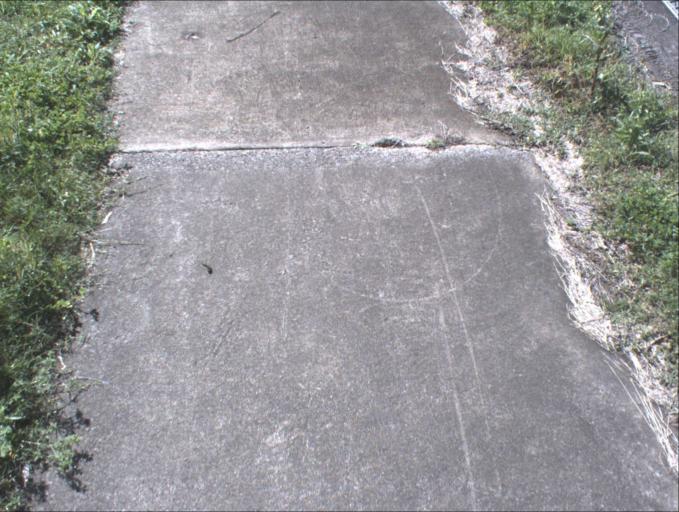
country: AU
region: Queensland
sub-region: Logan
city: North Maclean
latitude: -27.8259
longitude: 153.0312
